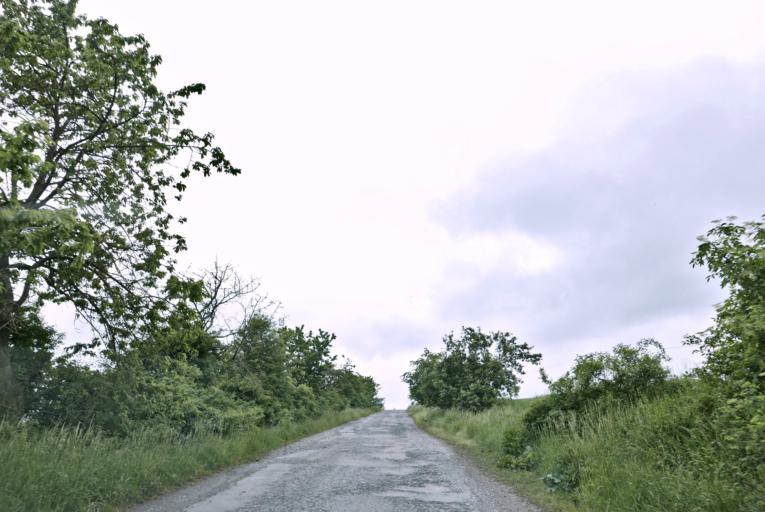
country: CZ
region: Plzensky
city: Zihle
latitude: 50.0073
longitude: 13.3336
